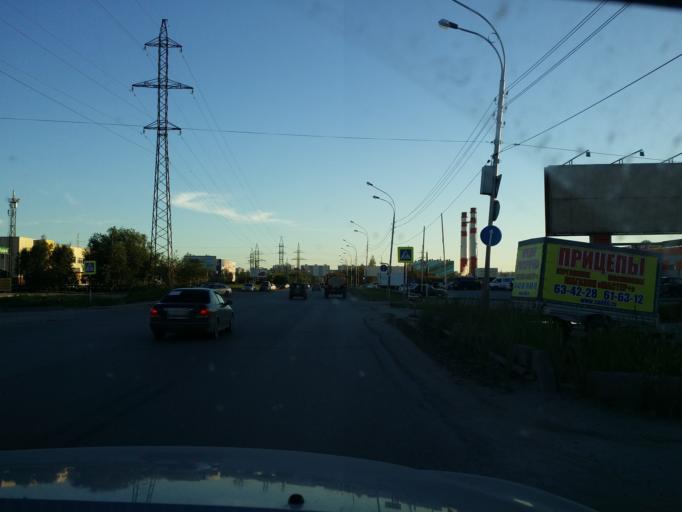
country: RU
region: Khanty-Mansiyskiy Avtonomnyy Okrug
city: Nizhnevartovsk
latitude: 60.9434
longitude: 76.6370
